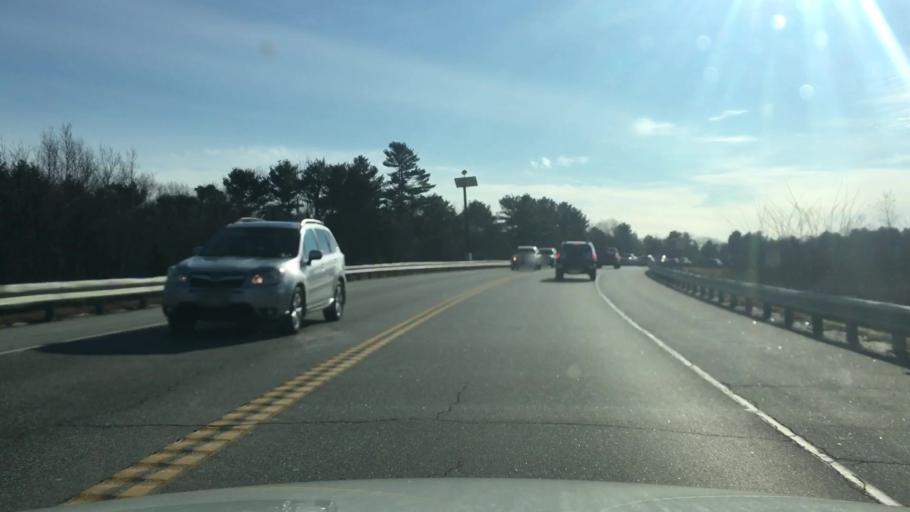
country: US
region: Maine
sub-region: Cumberland County
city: Brunswick
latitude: 43.9314
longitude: -69.9501
